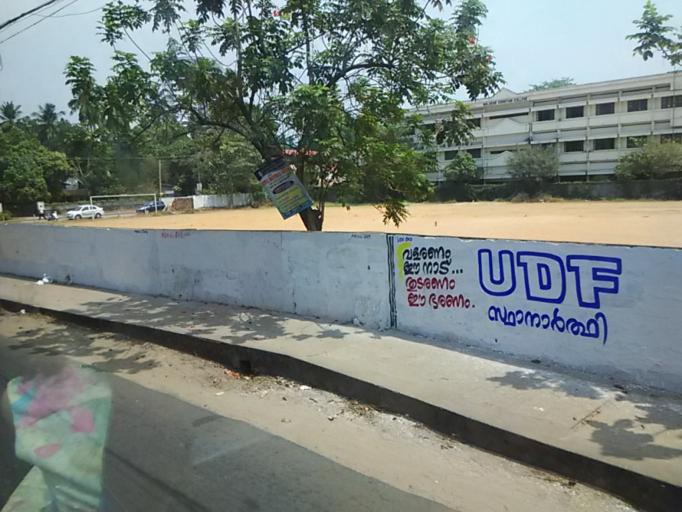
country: IN
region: Kerala
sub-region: Kozhikode
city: Kozhikode
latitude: 11.2636
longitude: 75.7774
